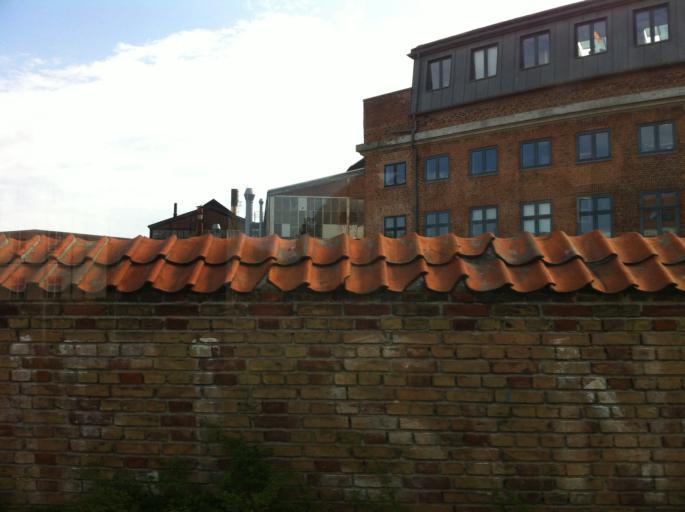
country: DK
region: Capital Region
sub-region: Helsingor Kommune
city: Helsingor
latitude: 56.0378
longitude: 12.6132
